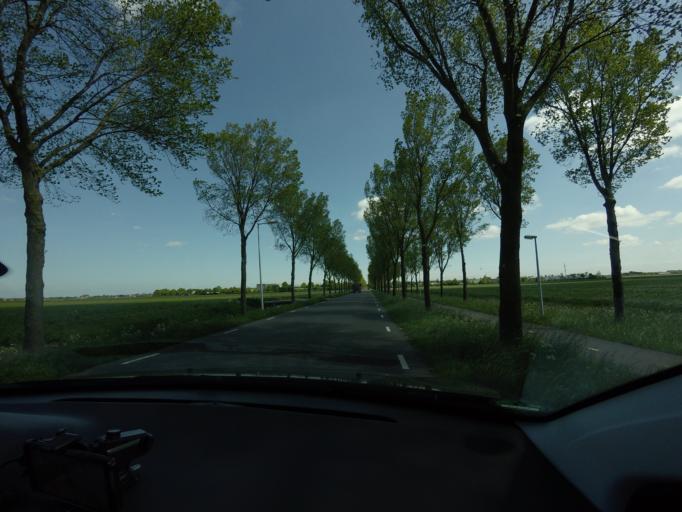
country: NL
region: North Holland
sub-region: Gemeente Beemster
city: Halfweg
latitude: 52.5526
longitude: 4.8938
